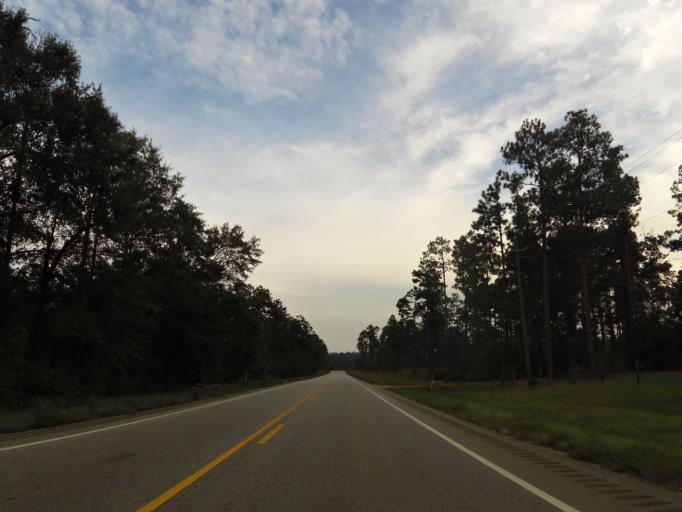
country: US
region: Alabama
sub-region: Monroe County
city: Frisco City
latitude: 31.2678
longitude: -87.4991
